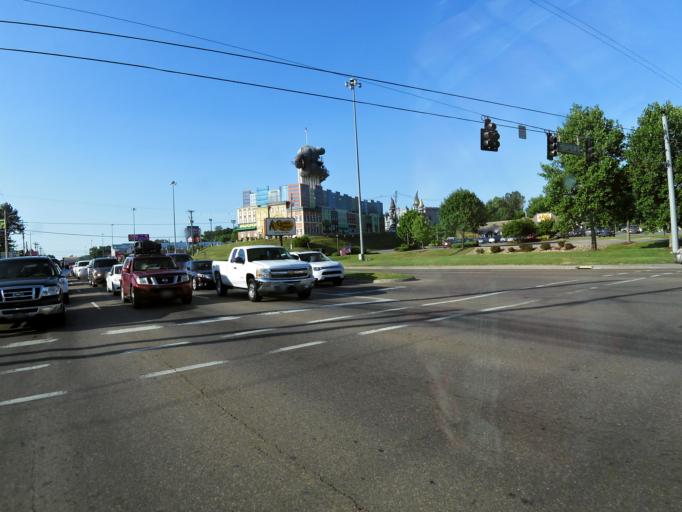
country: US
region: Tennessee
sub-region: Sevier County
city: Pigeon Forge
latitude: 35.8140
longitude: -83.5782
